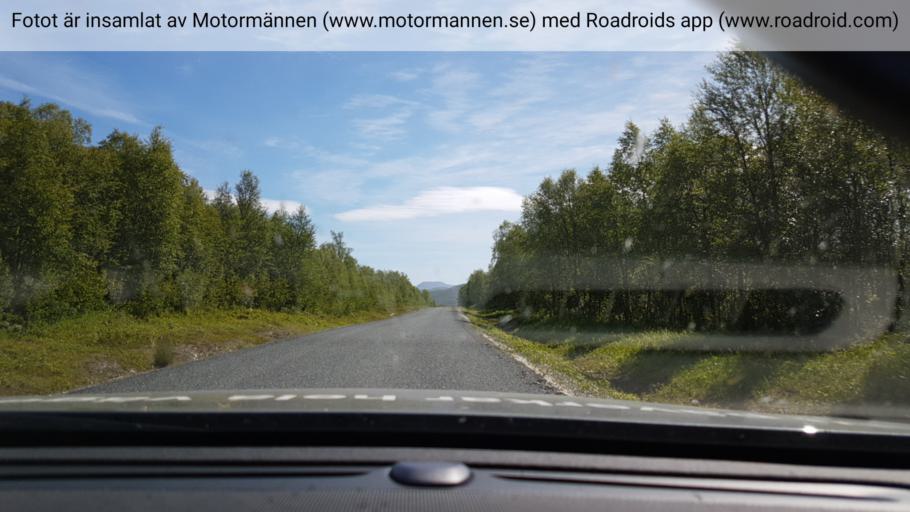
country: NO
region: Nordland
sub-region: Hattfjelldal
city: Hattfjelldal
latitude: 65.3360
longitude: 15.1241
